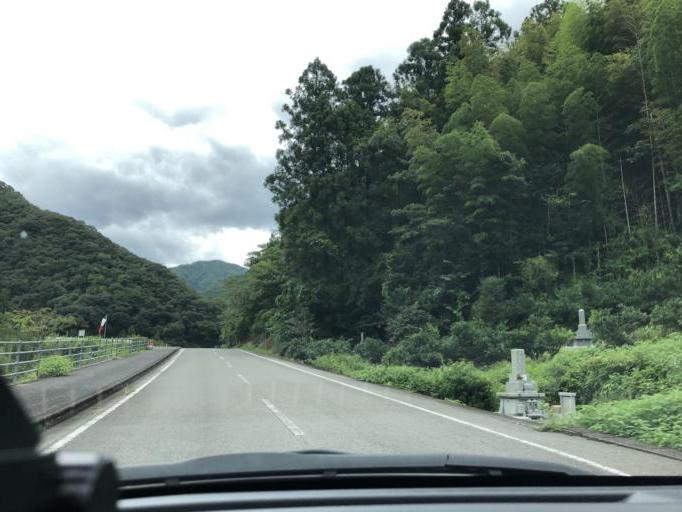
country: JP
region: Kochi
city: Kochi-shi
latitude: 33.6291
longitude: 133.5146
